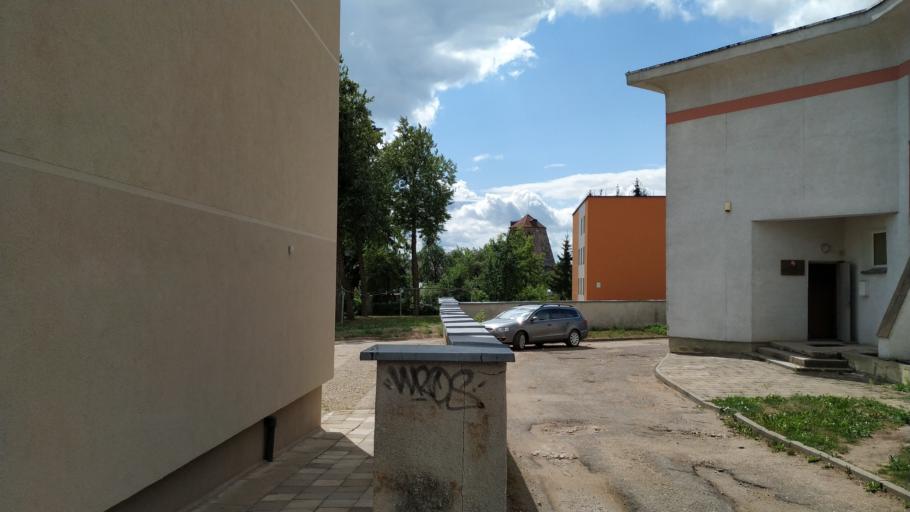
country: LT
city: Kupiskis
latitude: 55.8383
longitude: 24.9740
